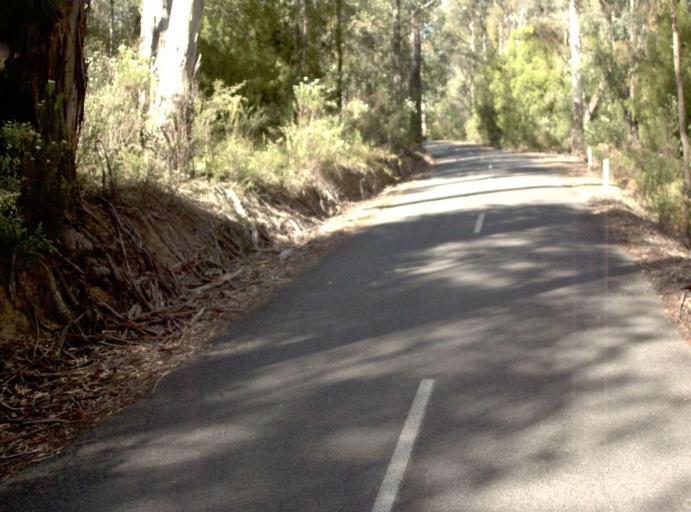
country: AU
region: Victoria
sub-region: East Gippsland
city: Lakes Entrance
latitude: -37.4573
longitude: 148.5715
